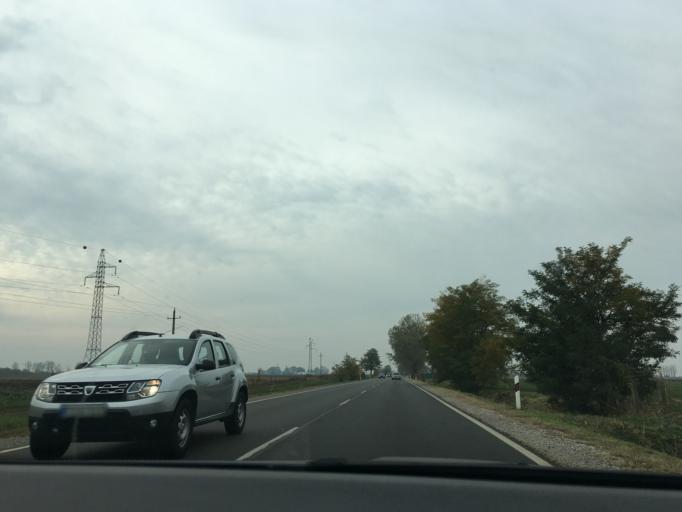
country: HU
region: Hajdu-Bihar
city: Barand
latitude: 47.3506
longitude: 21.2035
